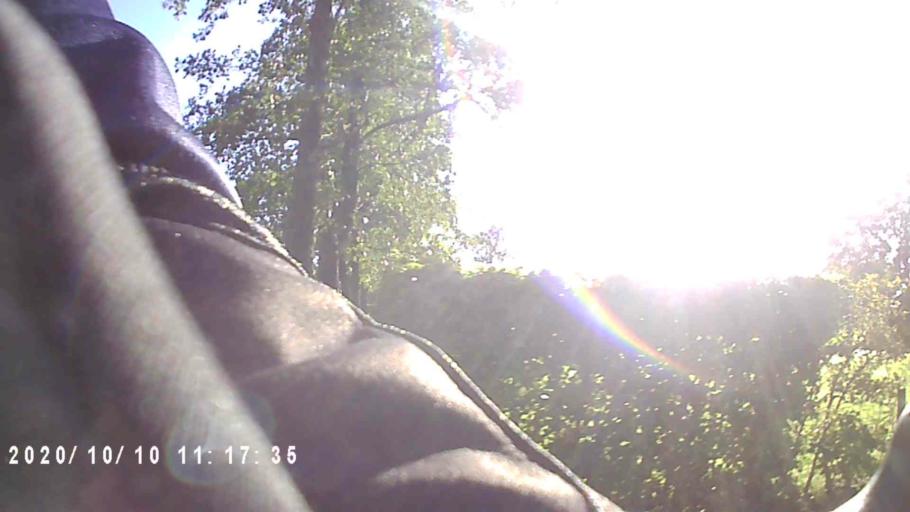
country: NL
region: Friesland
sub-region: Gemeente Smallingerland
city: Drachtstercompagnie
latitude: 53.0961
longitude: 6.1978
